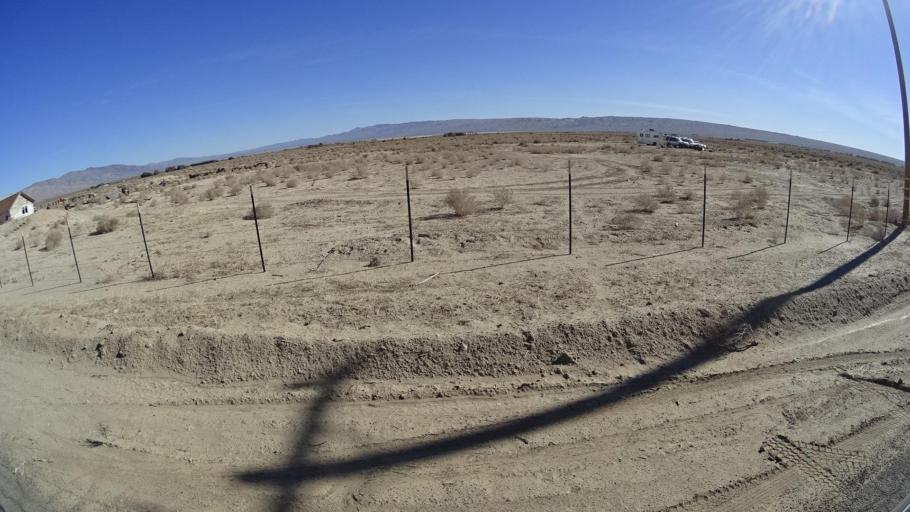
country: US
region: California
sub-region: Kern County
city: California City
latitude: 35.3025
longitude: -117.9682
